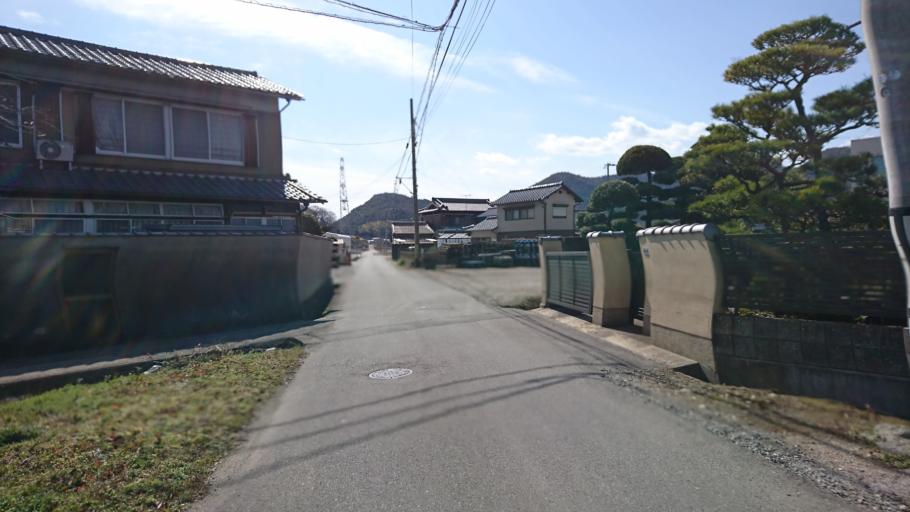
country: JP
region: Hyogo
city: Kakogawacho-honmachi
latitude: 34.8079
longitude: 134.8115
